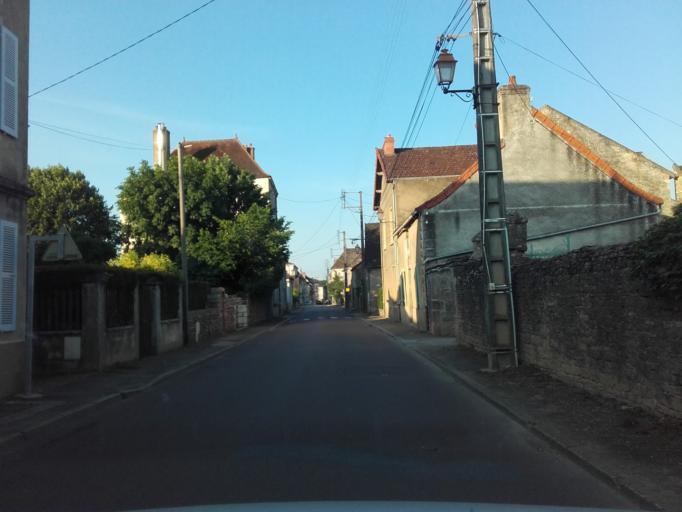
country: FR
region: Bourgogne
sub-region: Departement de Saone-et-Loire
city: Givry
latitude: 46.7856
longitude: 4.7444
